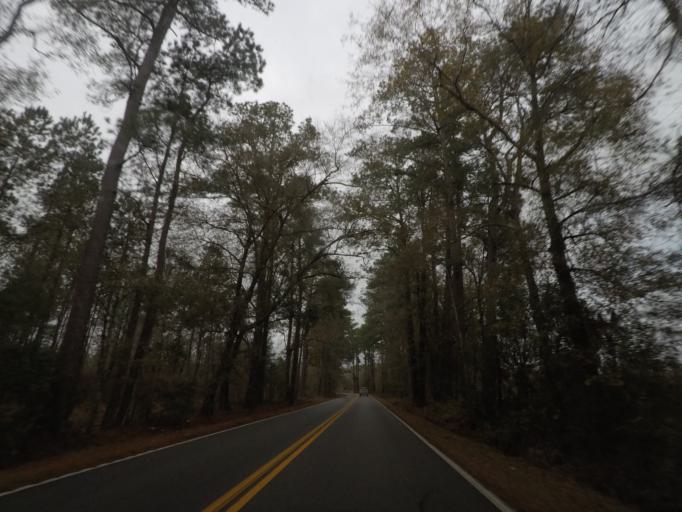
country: US
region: South Carolina
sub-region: Colleton County
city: Walterboro
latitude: 32.9333
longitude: -80.5389
